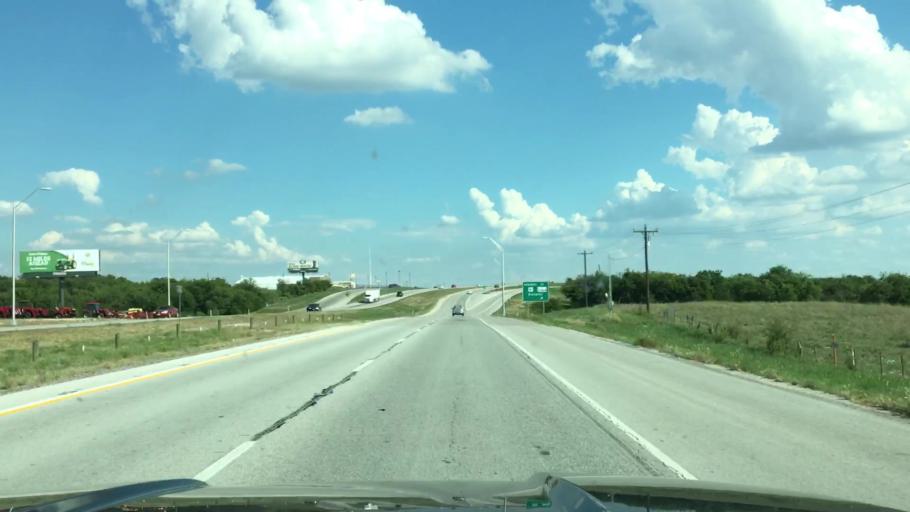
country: US
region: Texas
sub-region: Wise County
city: Decatur
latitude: 33.2092
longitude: -97.5743
